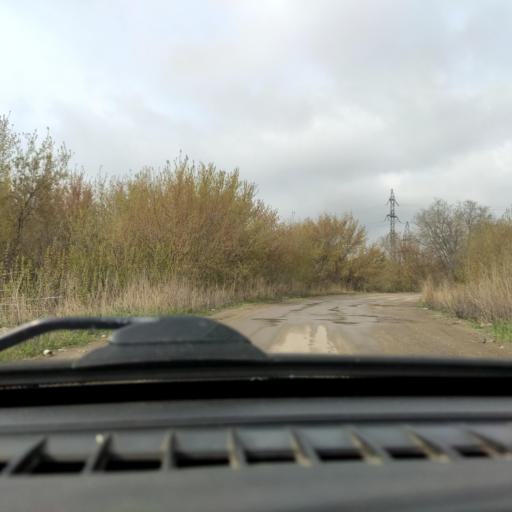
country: RU
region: Samara
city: Zhigulevsk
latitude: 53.5391
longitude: 49.4960
